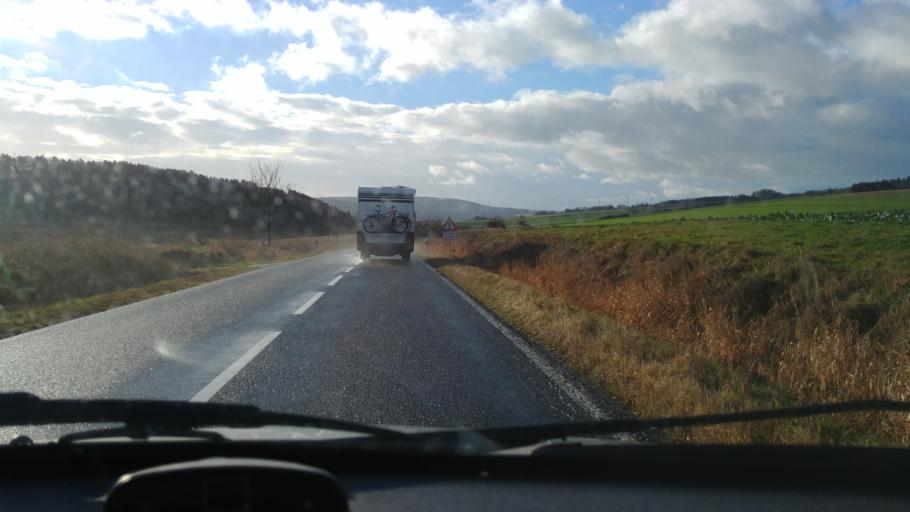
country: DE
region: Hesse
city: Taunusstein
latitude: 50.1685
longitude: 8.1855
